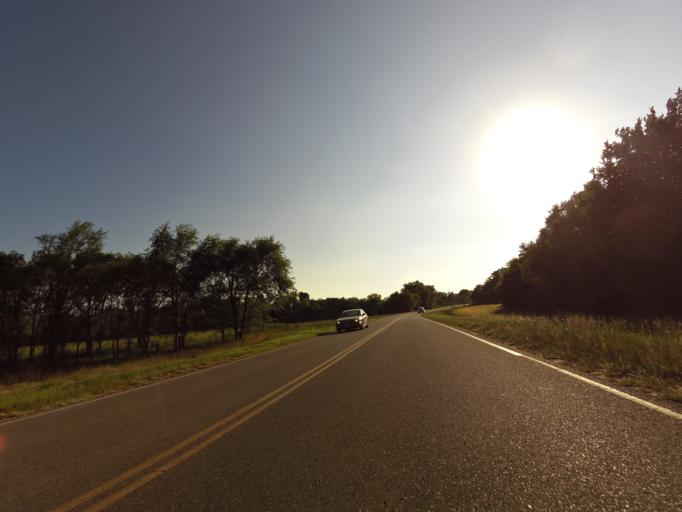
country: US
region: Kansas
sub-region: Reno County
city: Buhler
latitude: 38.1487
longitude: -97.8358
